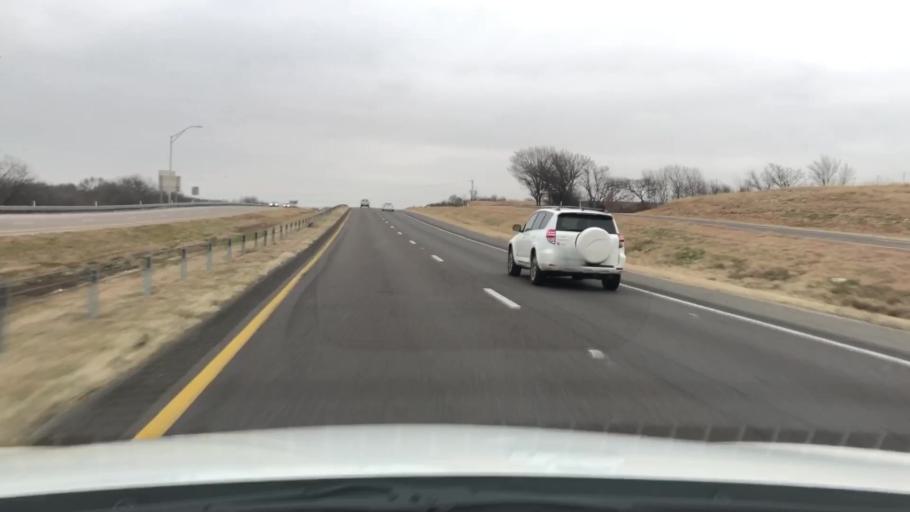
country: US
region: Texas
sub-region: Cooke County
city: Gainesville
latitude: 33.6959
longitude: -97.1625
